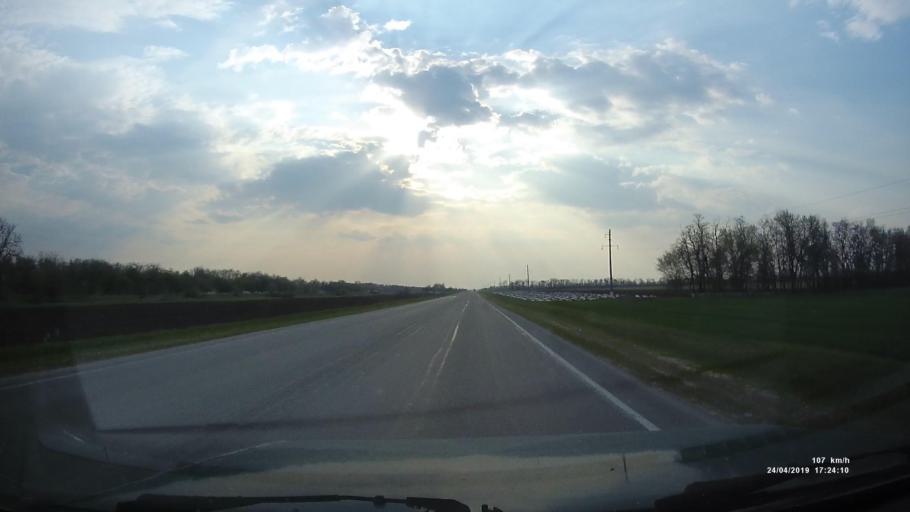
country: RU
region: Rostov
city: Gigant
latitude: 46.5234
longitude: 41.2688
